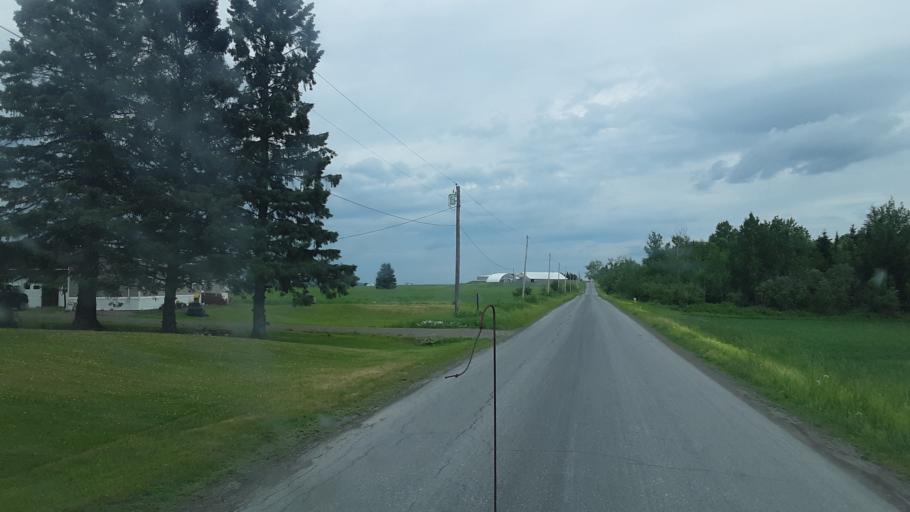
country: US
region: Maine
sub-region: Aroostook County
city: Easton
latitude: 46.6893
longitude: -67.8468
